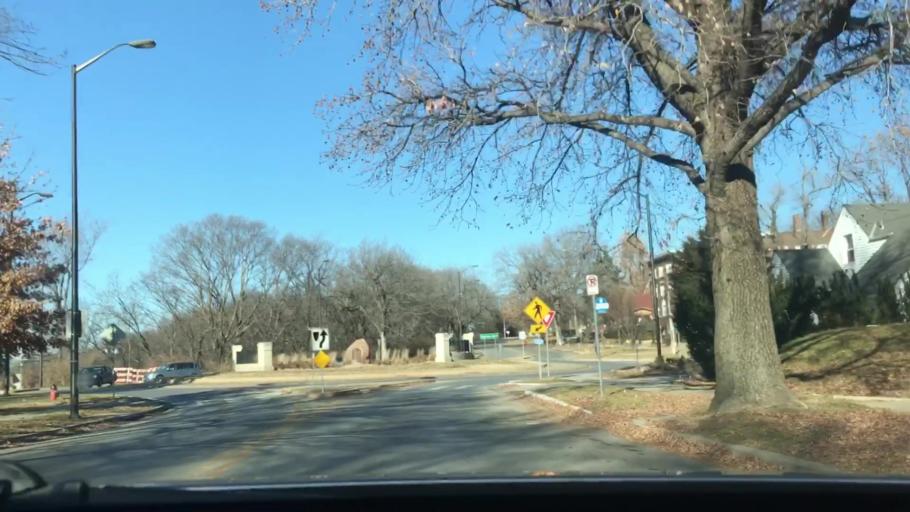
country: US
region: Missouri
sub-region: Clay County
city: North Kansas City
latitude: 39.1128
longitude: -94.5443
